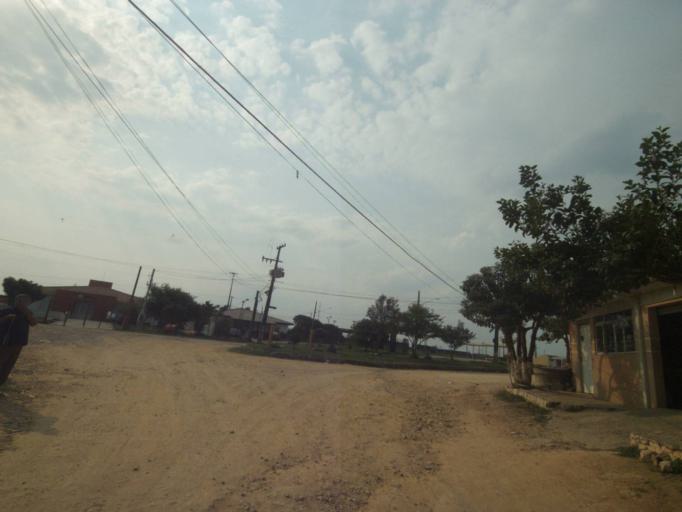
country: BR
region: Parana
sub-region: Sao Jose Dos Pinhais
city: Sao Jose dos Pinhais
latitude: -25.5369
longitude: -49.2321
